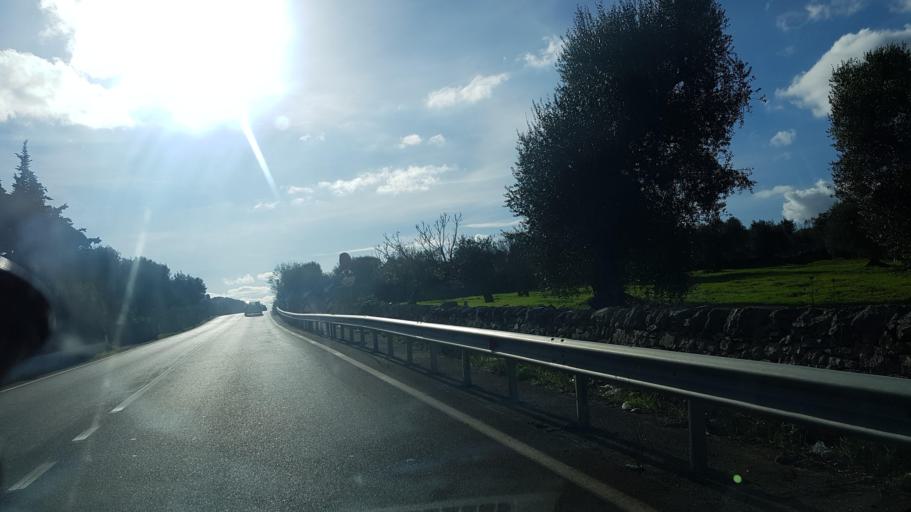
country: IT
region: Apulia
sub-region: Provincia di Brindisi
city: Ceglie Messapica
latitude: 40.6583
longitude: 17.5293
